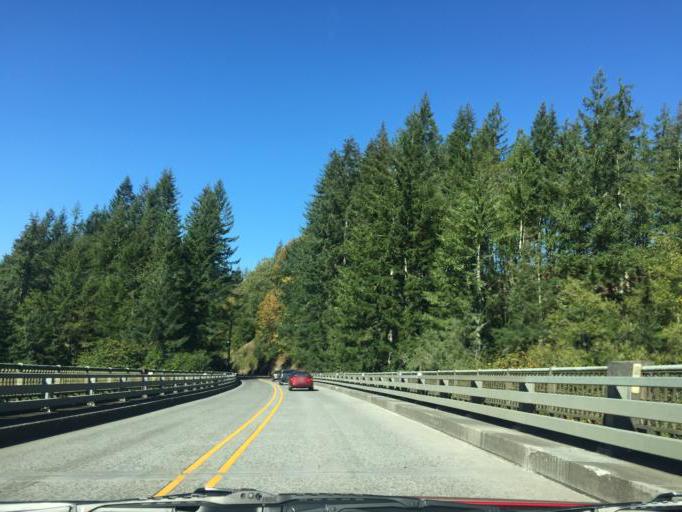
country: US
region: Oregon
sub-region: Columbia County
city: Vernonia
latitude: 45.8412
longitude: -123.5176
